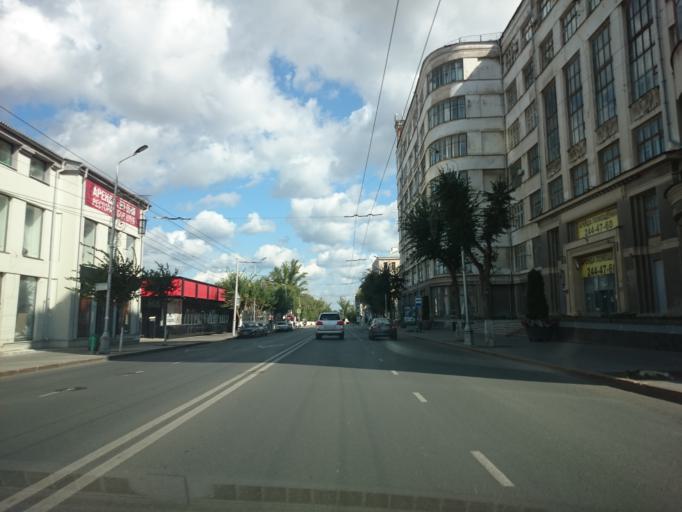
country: RU
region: Samara
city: Rozhdestveno
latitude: 53.1940
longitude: 50.0932
